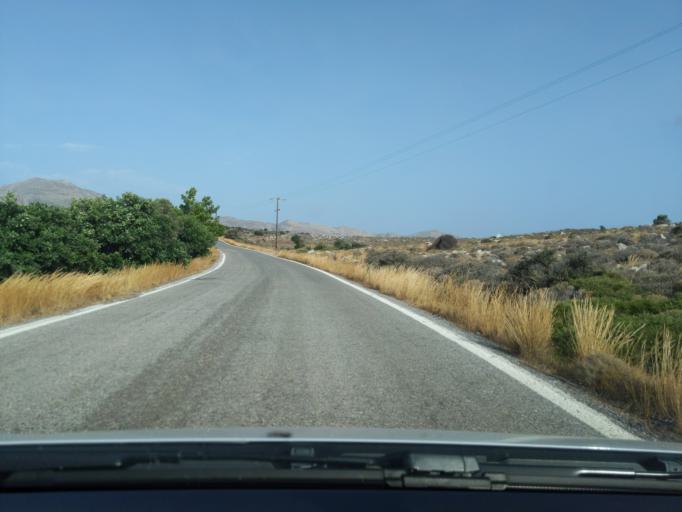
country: GR
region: Crete
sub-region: Nomos Lasithiou
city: Palekastro
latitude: 35.0879
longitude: 26.2423
